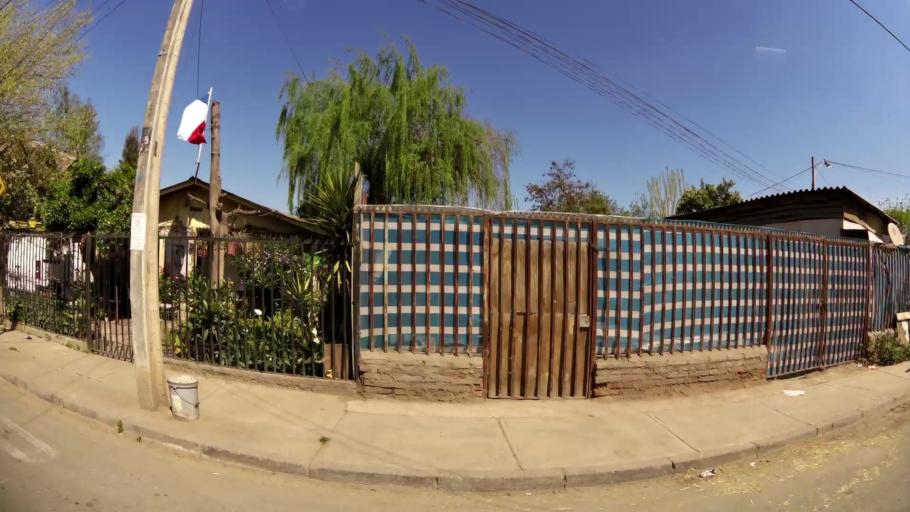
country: CL
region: Santiago Metropolitan
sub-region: Provincia de Santiago
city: Lo Prado
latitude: -33.4023
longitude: -70.7377
